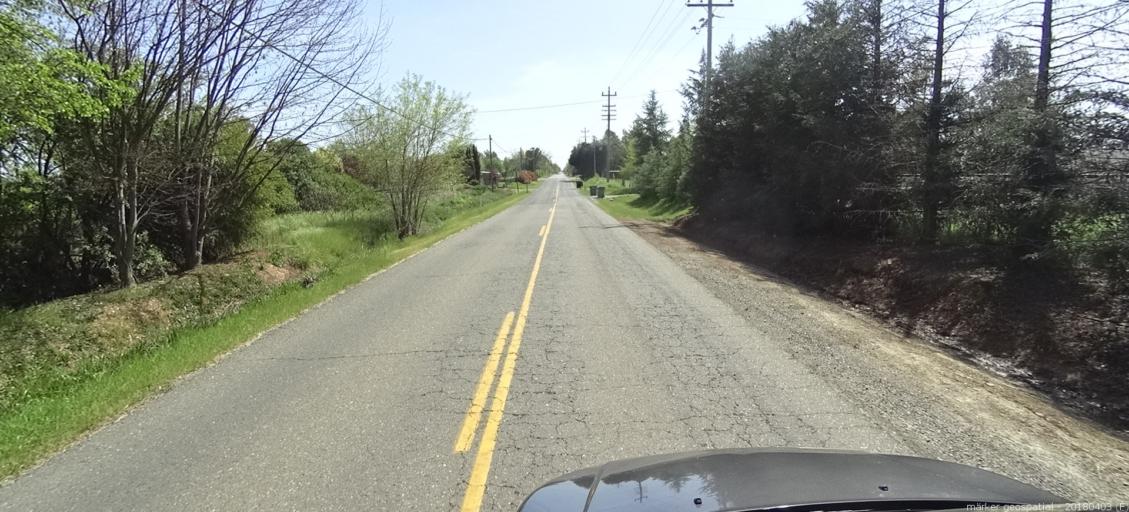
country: US
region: California
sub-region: Sacramento County
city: Herald
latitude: 38.3447
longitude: -121.2421
